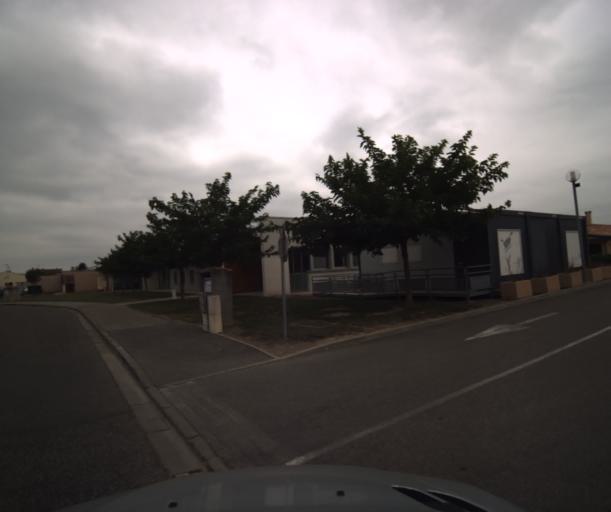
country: FR
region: Midi-Pyrenees
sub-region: Departement de la Haute-Garonne
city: Portet-sur-Garonne
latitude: 43.5207
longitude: 1.3998
